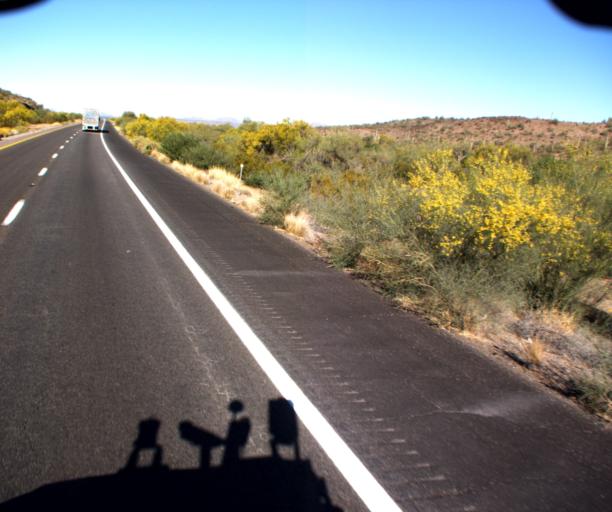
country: US
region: Arizona
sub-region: Pinal County
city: Maricopa
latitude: 32.8356
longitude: -112.1853
